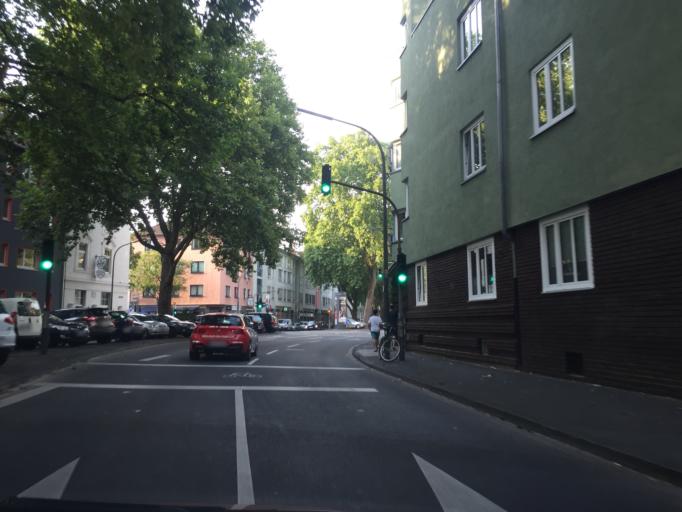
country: DE
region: North Rhine-Westphalia
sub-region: Regierungsbezirk Koln
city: Neustadt/Sued
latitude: 50.9118
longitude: 6.9457
